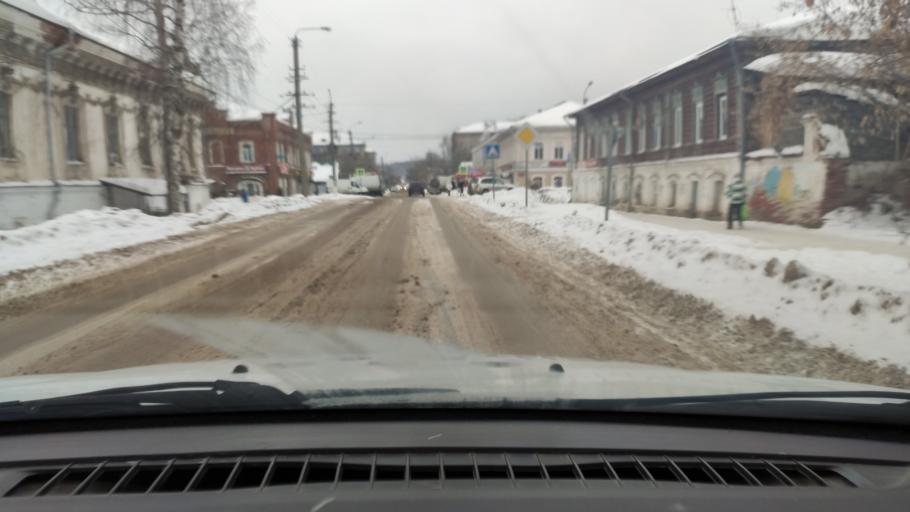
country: RU
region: Perm
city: Kungur
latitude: 57.4381
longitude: 56.9369
